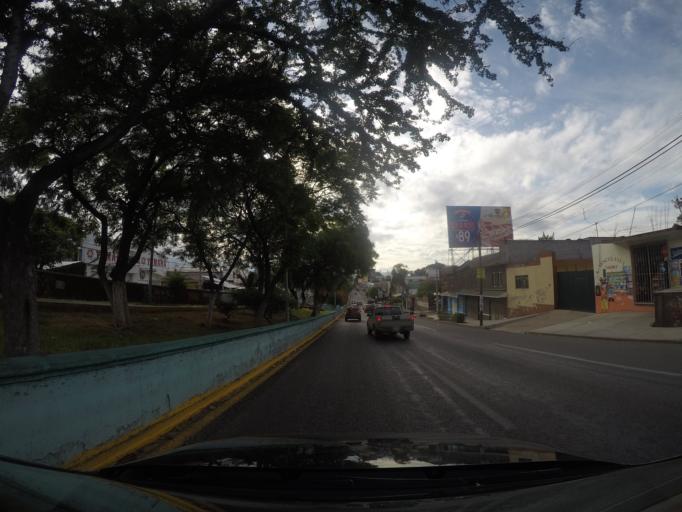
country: MX
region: Oaxaca
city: Oaxaca de Juarez
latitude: 17.0701
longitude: -96.7099
